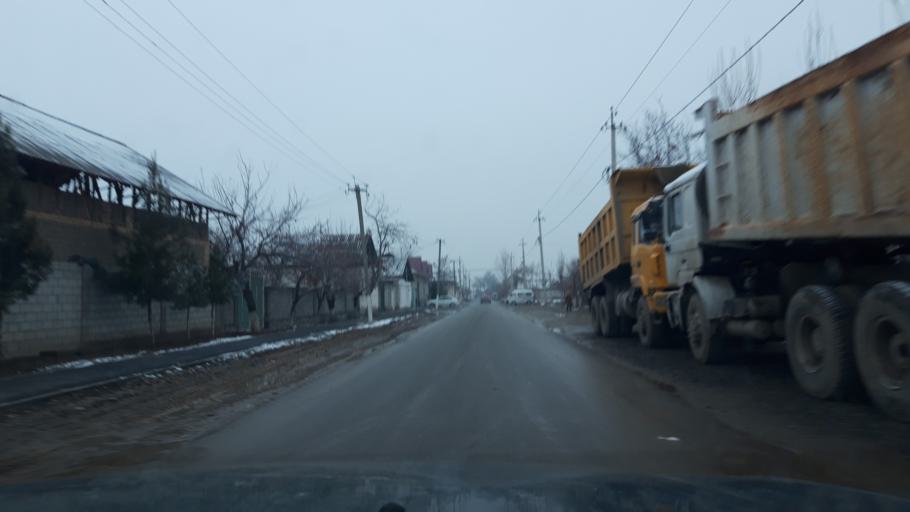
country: UZ
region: Andijon
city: Andijon
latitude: 40.7407
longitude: 72.2572
